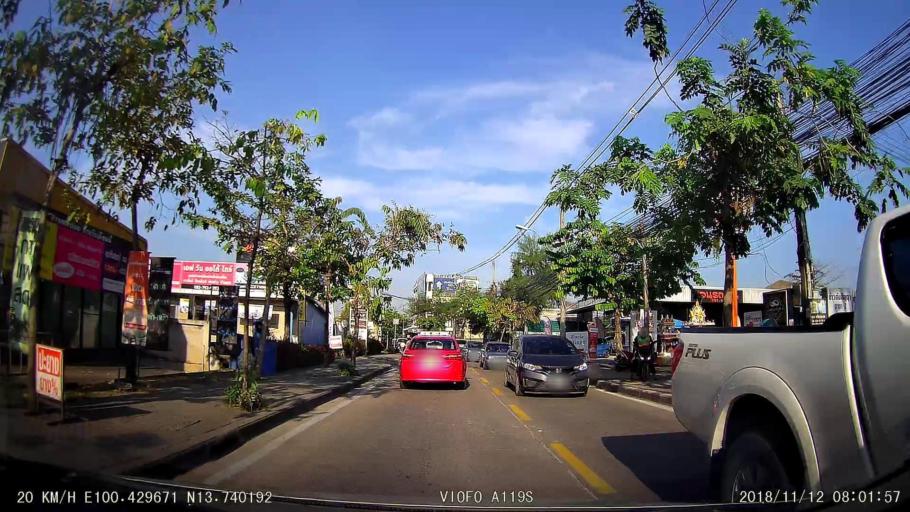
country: TH
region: Bangkok
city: Phasi Charoen
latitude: 13.7402
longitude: 100.4296
